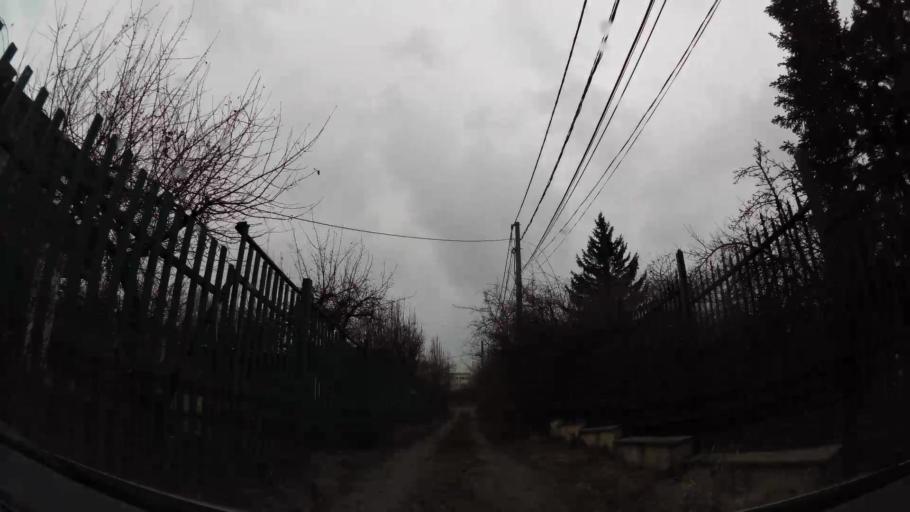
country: BG
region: Sofia-Capital
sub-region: Stolichna Obshtina
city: Sofia
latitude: 42.6158
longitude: 23.3595
